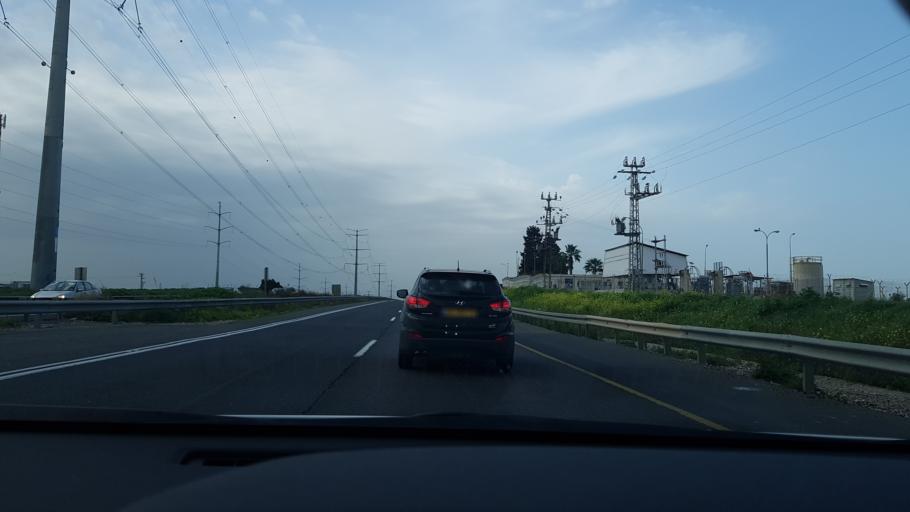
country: IL
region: Central District
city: Gan Yavne
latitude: 31.8017
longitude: 34.6903
